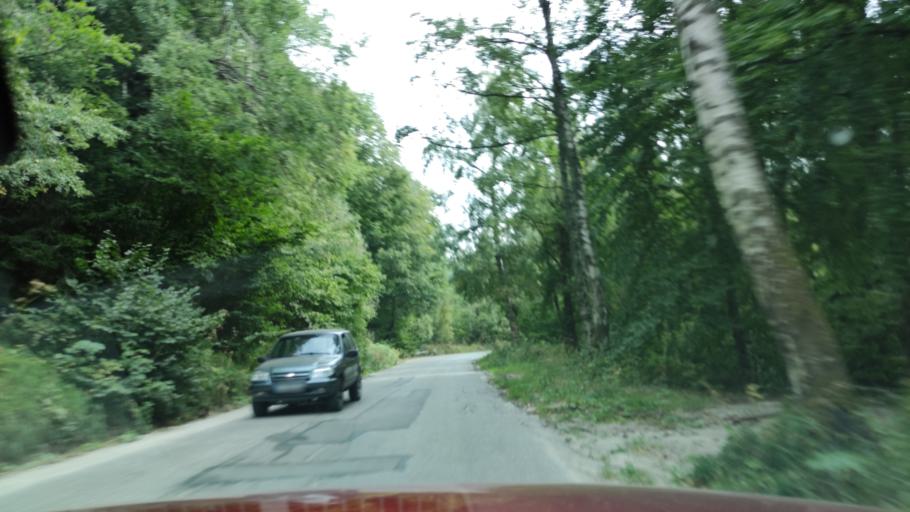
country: BG
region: Sofia-Capital
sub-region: Stolichna Obshtina
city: Sofia
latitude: 42.6144
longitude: 23.2323
